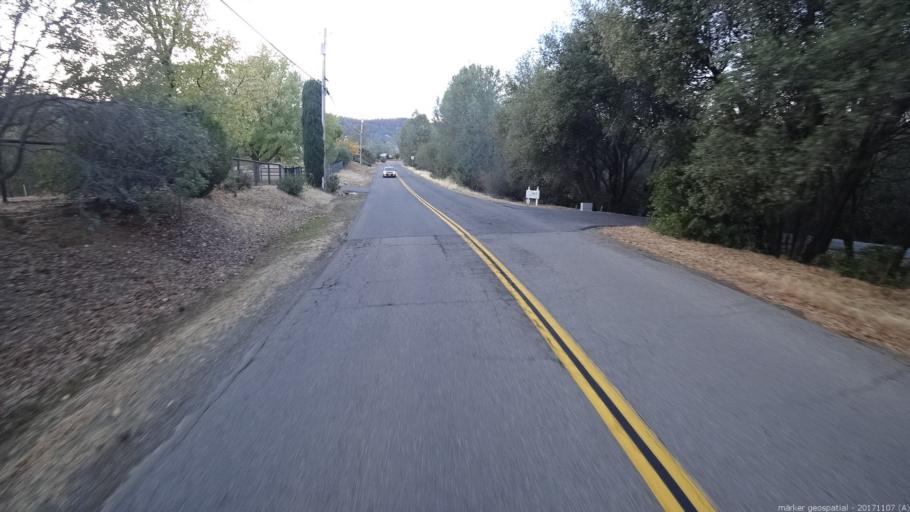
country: US
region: California
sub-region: Shasta County
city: Shasta
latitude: 40.5421
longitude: -122.4842
